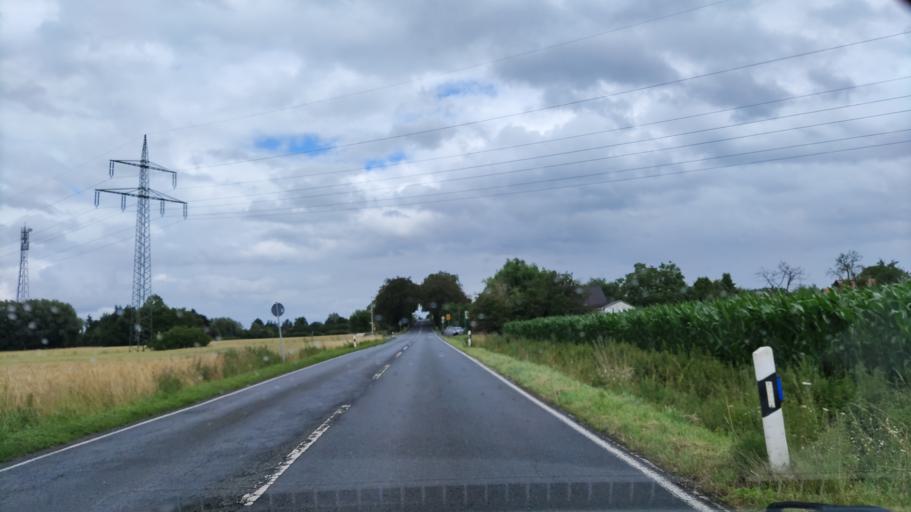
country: DE
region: North Rhine-Westphalia
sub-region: Regierungsbezirk Arnsberg
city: Welver
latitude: 51.6601
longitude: 7.9190
